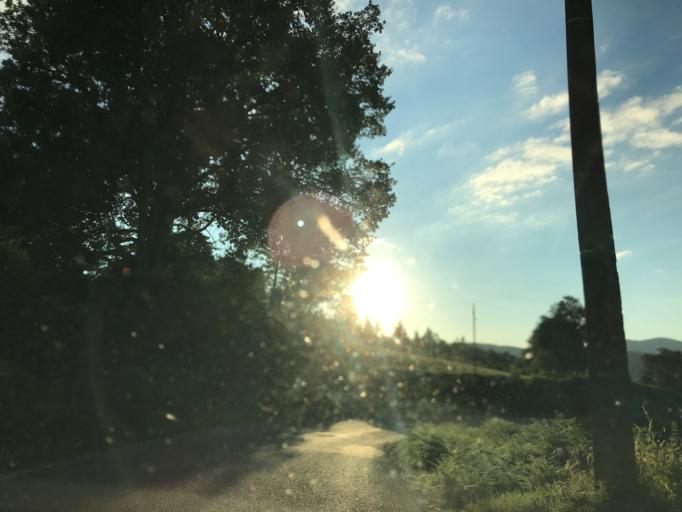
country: FR
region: Rhone-Alpes
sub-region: Departement de la Loire
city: Noiretable
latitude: 45.7913
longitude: 3.7780
